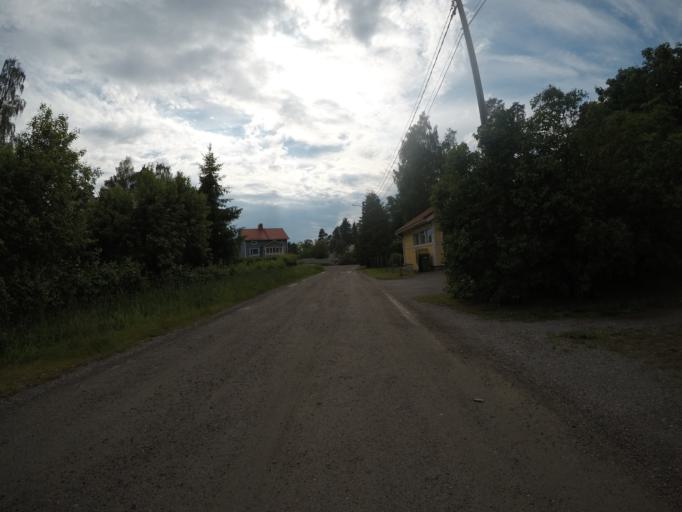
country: FI
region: Haeme
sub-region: Haemeenlinna
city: Haemeenlinna
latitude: 61.0126
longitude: 24.4815
